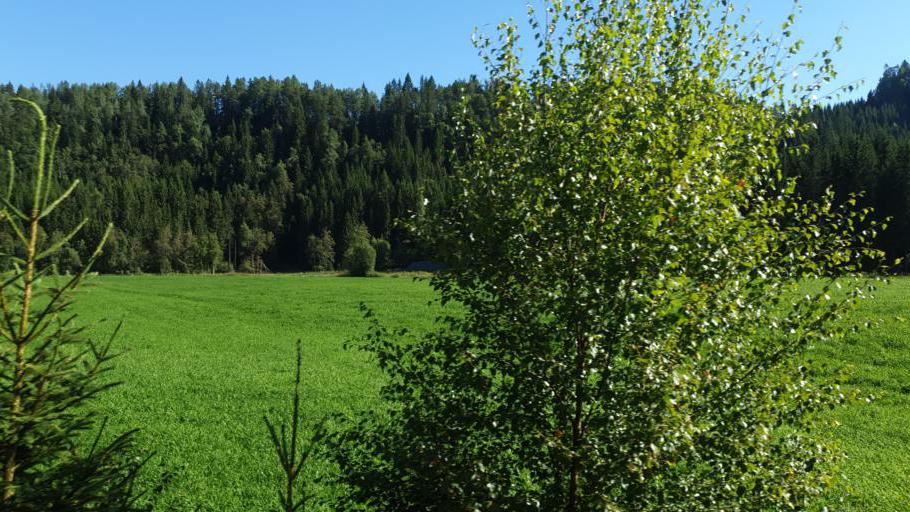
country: NO
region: Sor-Trondelag
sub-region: Meldal
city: Meldal
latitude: 63.1777
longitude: 9.7576
